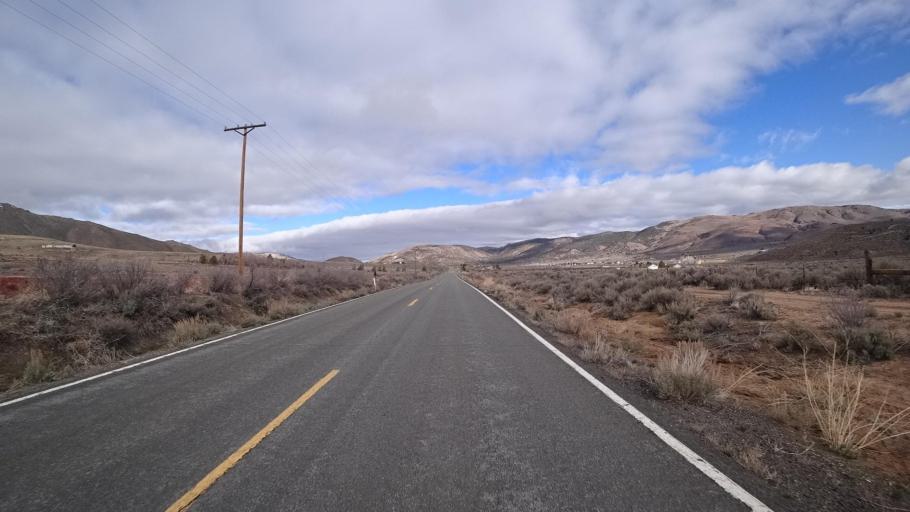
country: US
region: Nevada
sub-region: Washoe County
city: Cold Springs
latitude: 39.8780
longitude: -119.9658
